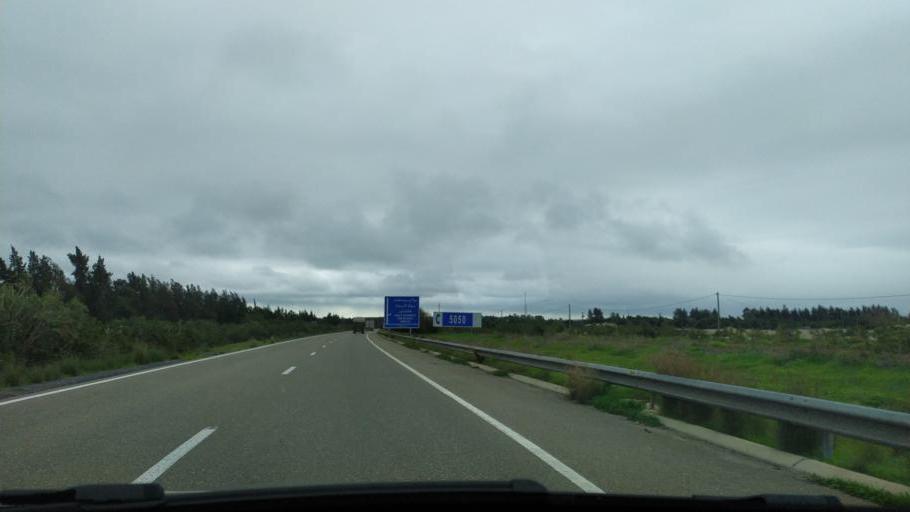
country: MA
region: Gharb-Chrarda-Beni Hssen
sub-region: Kenitra Province
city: Lalla Mimouna
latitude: 34.8863
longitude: -6.2106
